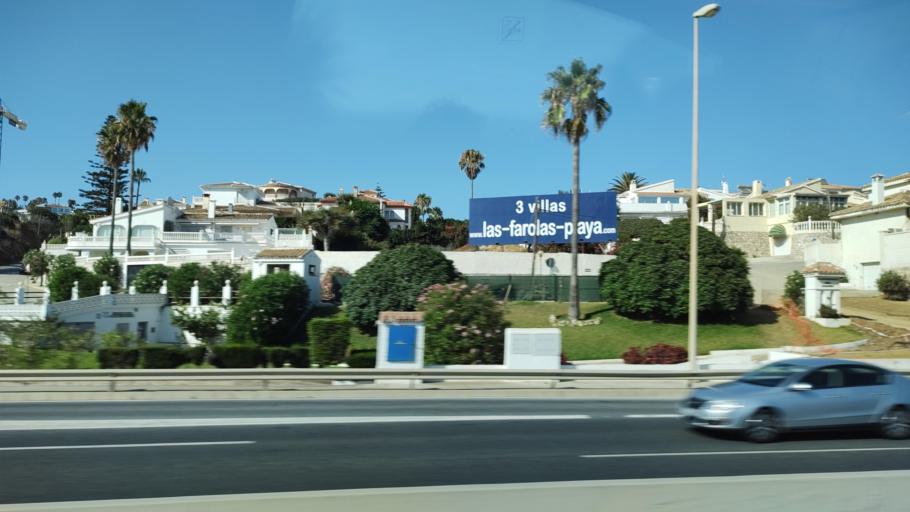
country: ES
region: Andalusia
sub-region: Provincia de Malaga
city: Fuengirola
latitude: 36.5067
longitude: -4.6563
